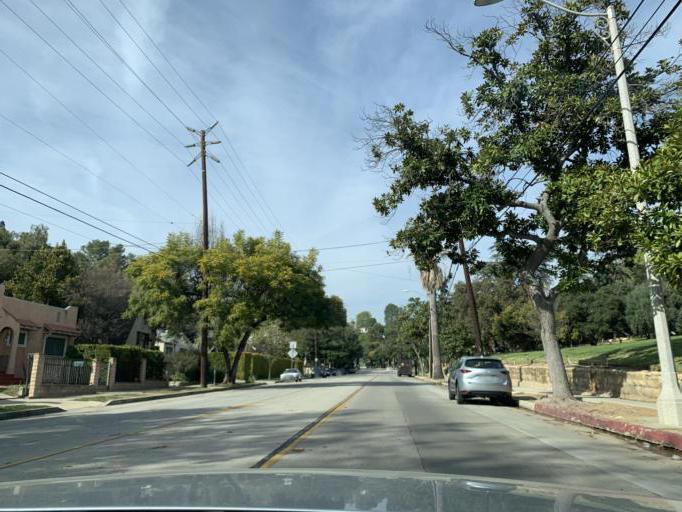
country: US
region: California
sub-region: Los Angeles County
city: South Pasadena
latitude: 34.1253
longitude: -118.1767
